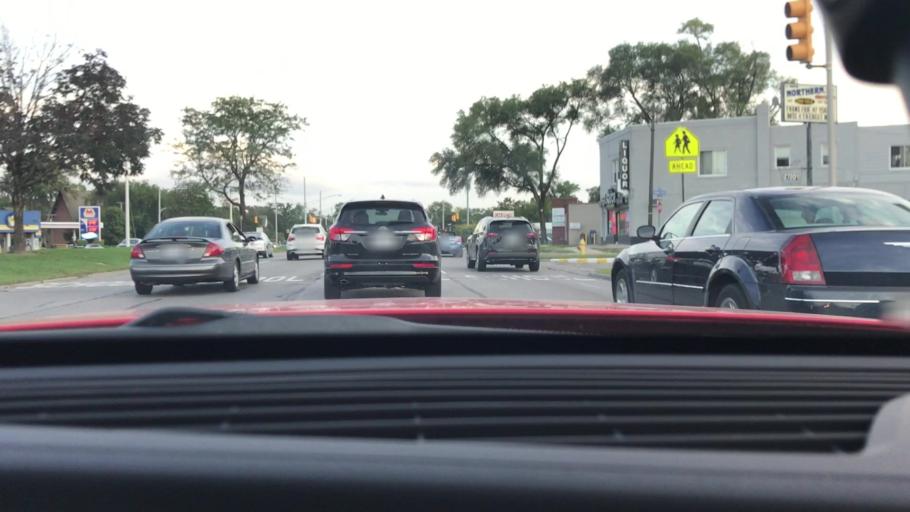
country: US
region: Michigan
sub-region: Oakland County
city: Huntington Woods
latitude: 42.4906
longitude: -83.1601
